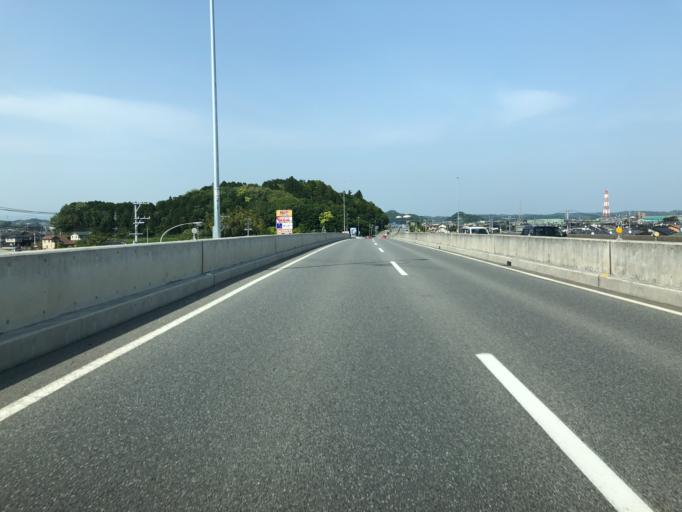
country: JP
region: Fukushima
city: Iwaki
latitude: 36.9387
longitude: 140.8558
